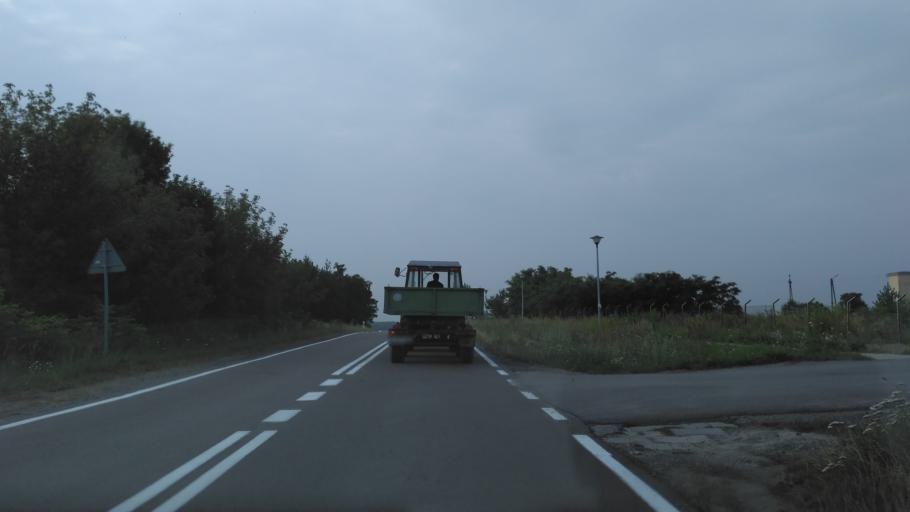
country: PL
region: Lublin Voivodeship
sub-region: Powiat chelmski
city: Rejowiec Fabryczny
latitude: 51.1813
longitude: 23.1749
